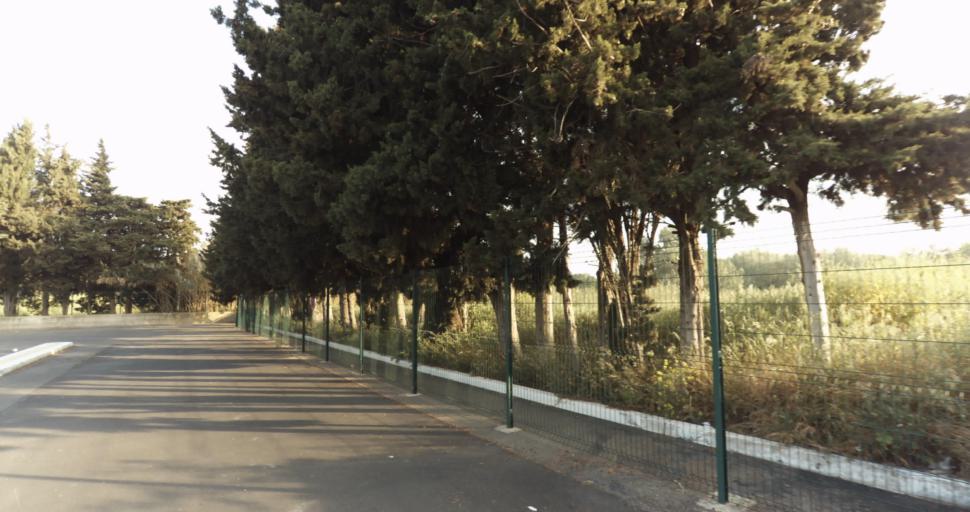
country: FR
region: Languedoc-Roussillon
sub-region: Departement du Gard
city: Caissargues
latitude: 43.8192
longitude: 4.3912
